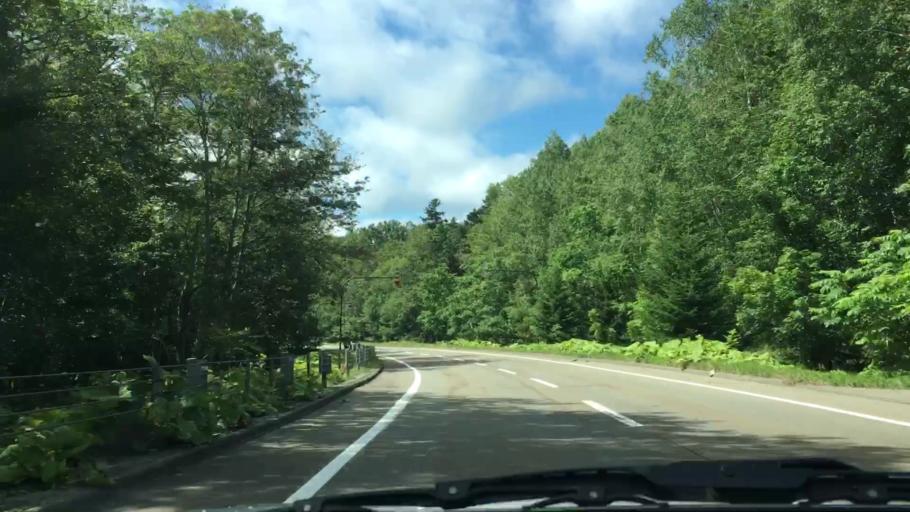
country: JP
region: Hokkaido
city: Kitami
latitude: 43.4042
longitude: 143.9347
